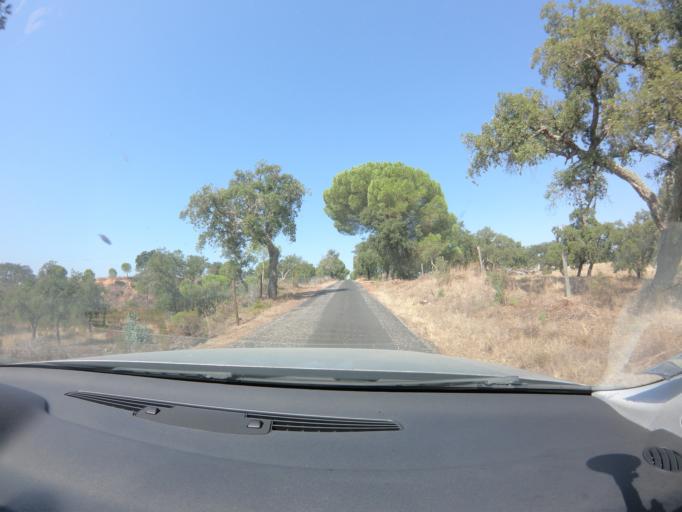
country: PT
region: Setubal
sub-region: Alcacer do Sal
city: Alcacer do Sal
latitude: 38.2536
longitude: -8.2992
